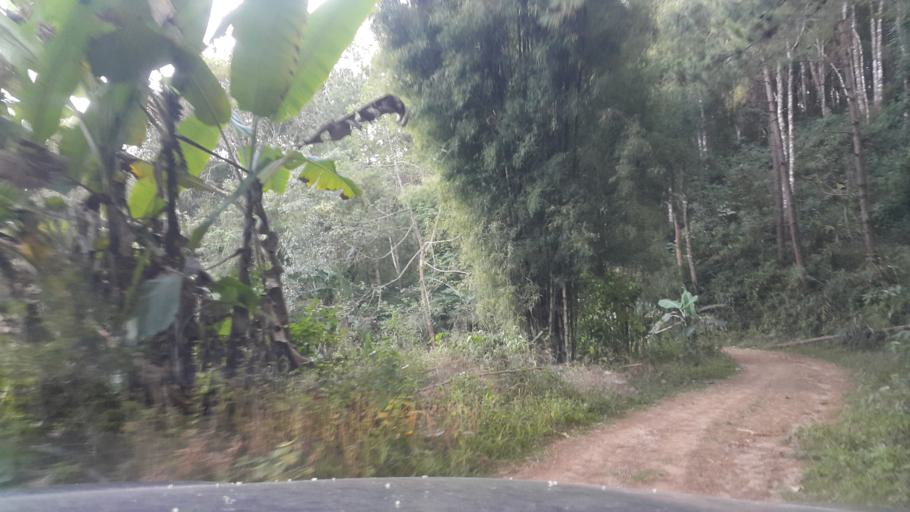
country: TH
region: Chiang Mai
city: Samoeng
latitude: 19.0155
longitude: 98.6493
